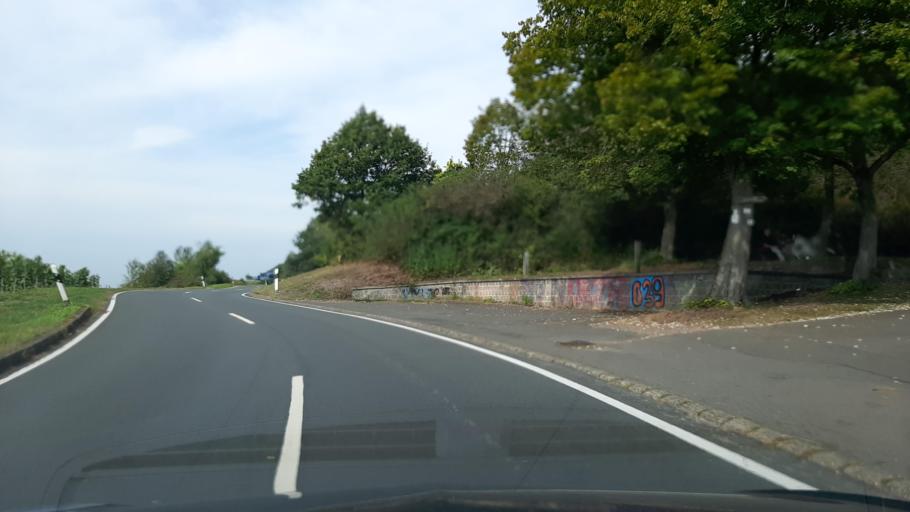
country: DE
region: Rheinland-Pfalz
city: Kinheim
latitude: 49.9810
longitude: 7.0498
